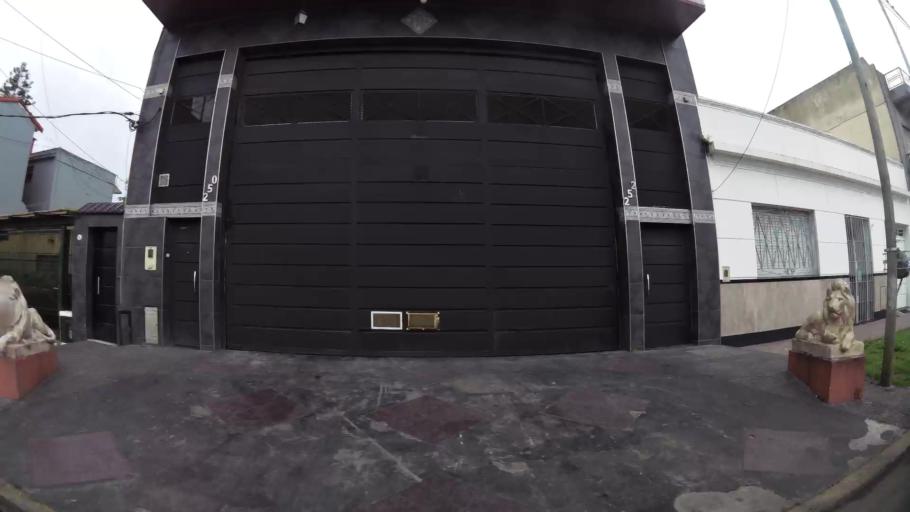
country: AR
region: Buenos Aires
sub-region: Partido de Avellaneda
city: Avellaneda
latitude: -34.6748
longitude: -58.3455
